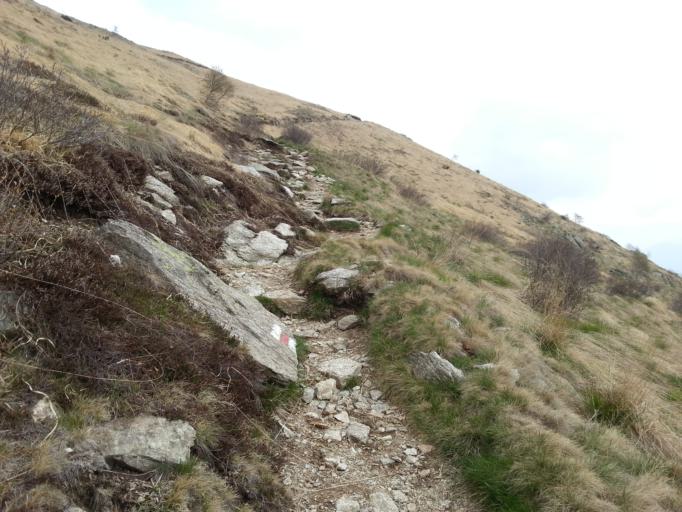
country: IT
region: Lombardy
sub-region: Provincia di Varese
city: Curiglia
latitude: 46.0462
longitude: 8.8412
